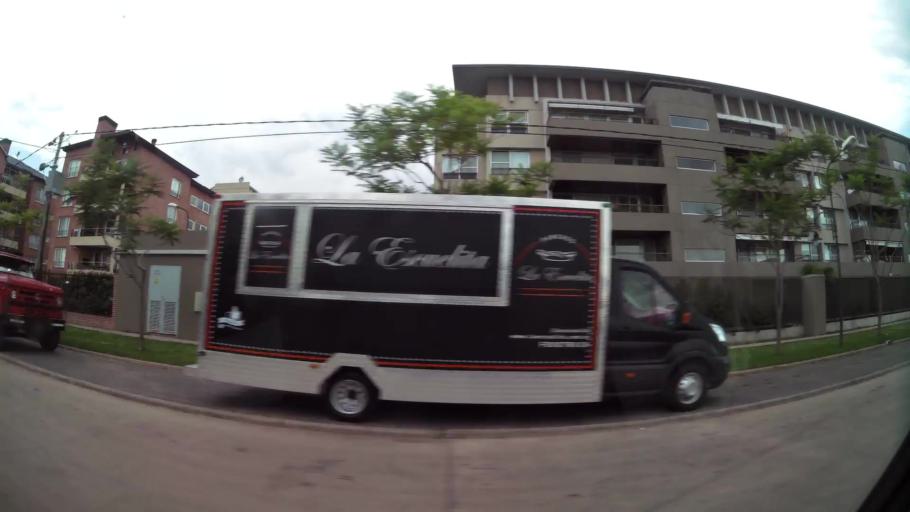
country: AR
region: Buenos Aires
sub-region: Partido de Tigre
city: Tigre
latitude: -34.4812
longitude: -58.5886
